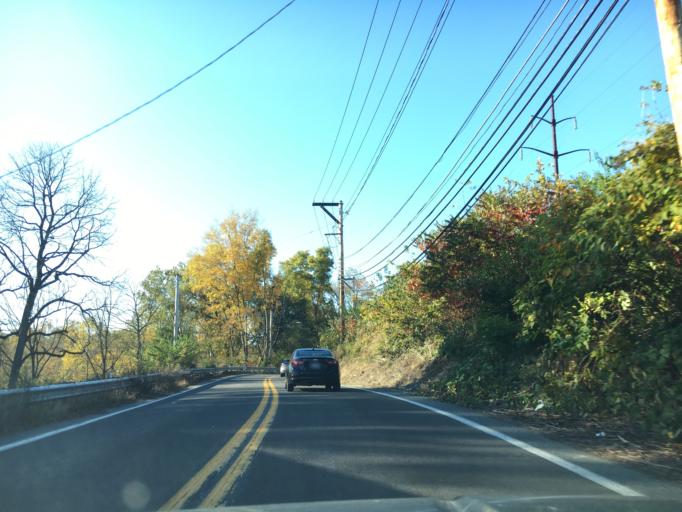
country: US
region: Pennsylvania
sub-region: Lehigh County
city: Fullerton
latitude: 40.6413
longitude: -75.4615
